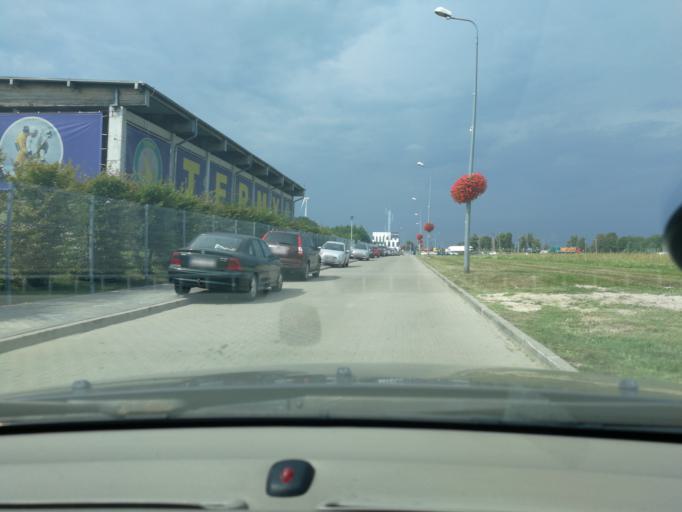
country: PL
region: Masovian Voivodeship
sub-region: Powiat zyrardowski
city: Mszczonow
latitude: 51.9779
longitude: 20.5268
